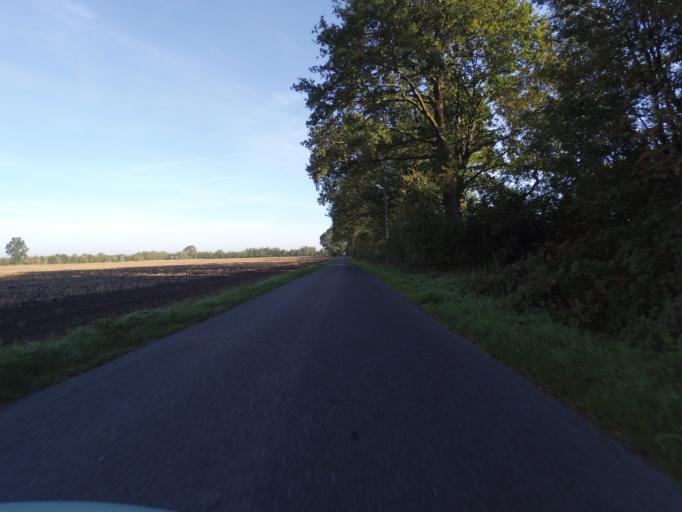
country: NL
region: Gelderland
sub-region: Gemeente Winterswijk
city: Winterswijk
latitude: 52.0544
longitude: 6.7212
